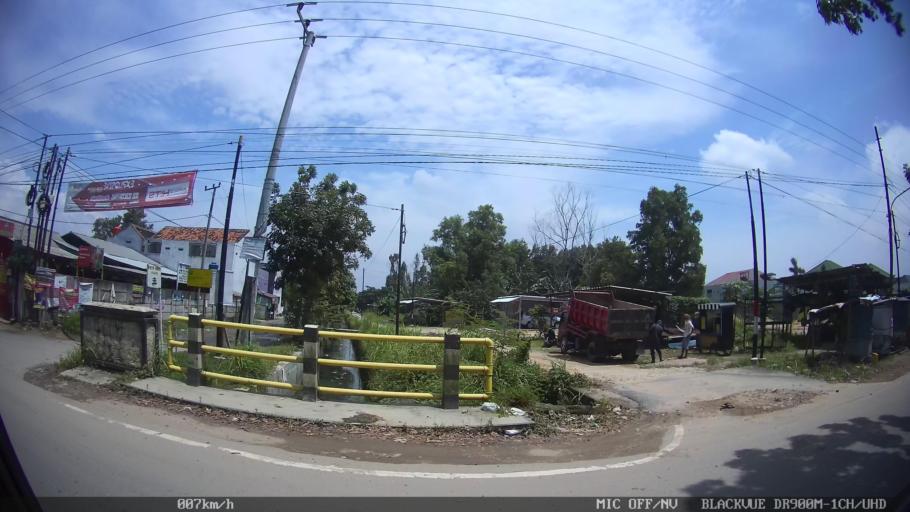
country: ID
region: Lampung
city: Kedaton
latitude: -5.3800
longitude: 105.3014
